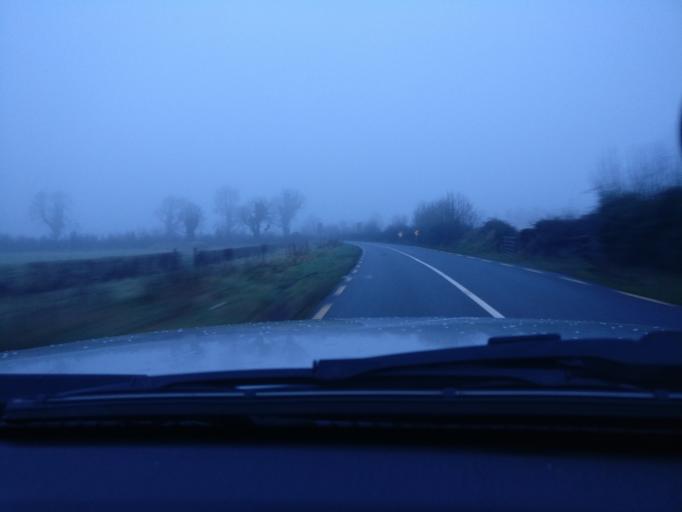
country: IE
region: Leinster
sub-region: An Mhi
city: Athboy
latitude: 53.6294
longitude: -6.9024
